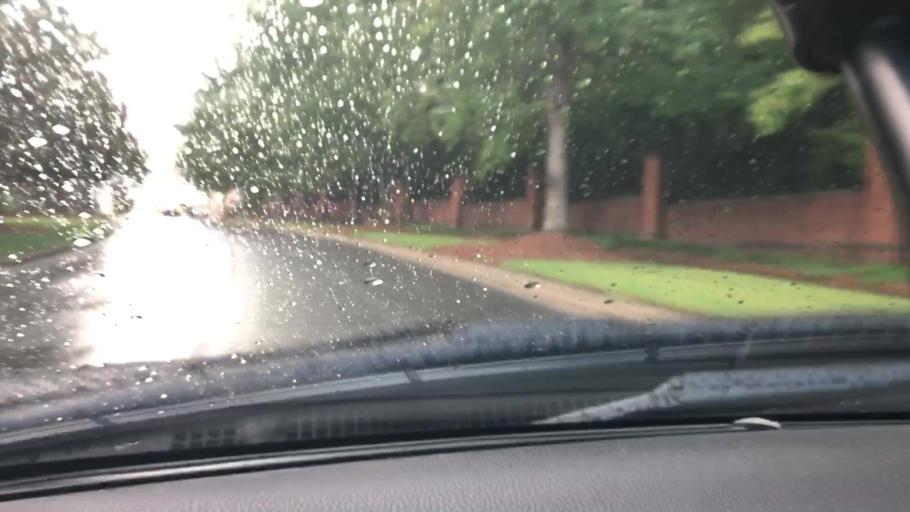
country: US
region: North Carolina
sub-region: Mecklenburg County
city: Charlotte
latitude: 35.1495
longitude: -80.8239
